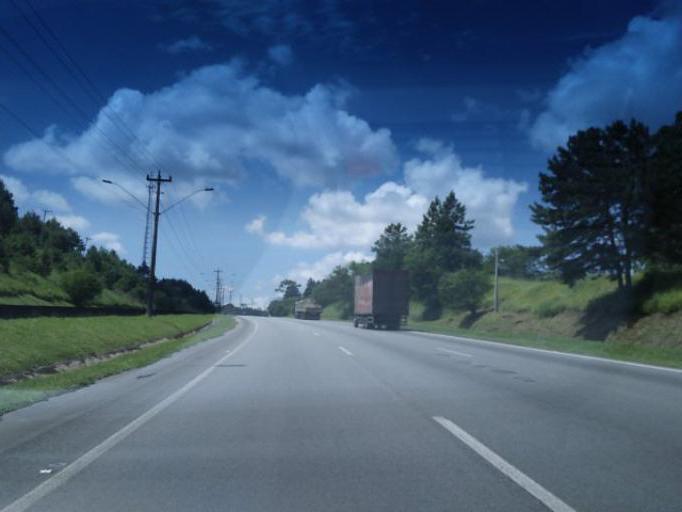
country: BR
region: Sao Paulo
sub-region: Sao Lourenco Da Serra
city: Sao Lourenco da Serra
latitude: -23.8230
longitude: -46.9256
